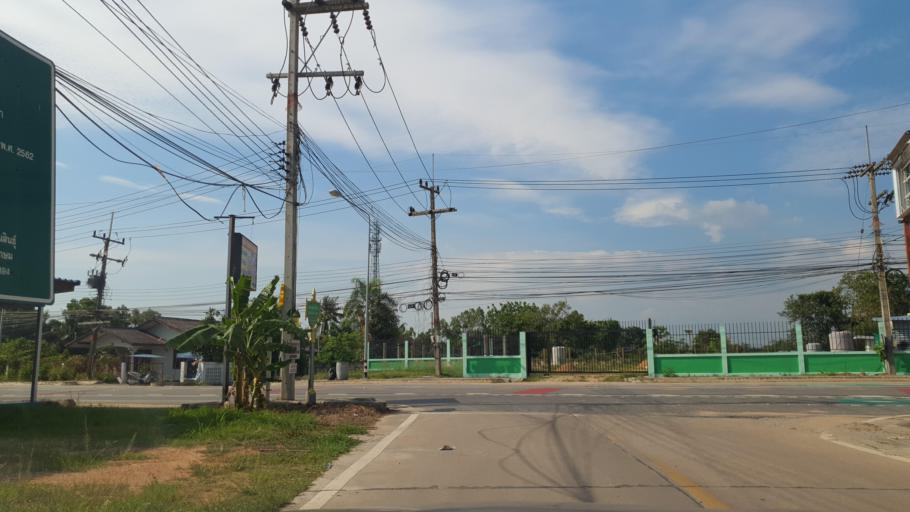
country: TH
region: Chon Buri
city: Phatthaya
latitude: 12.8053
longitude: 100.9315
